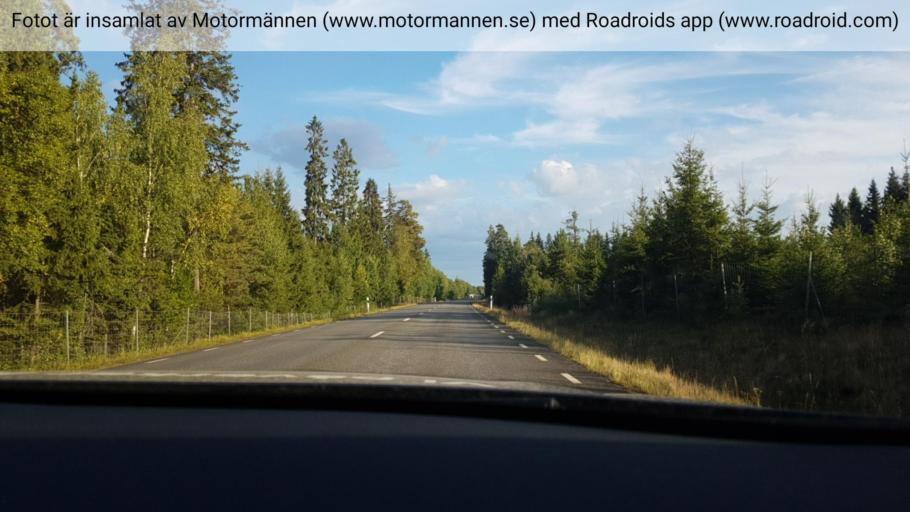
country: SE
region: Vaestra Goetaland
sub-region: Skara Kommun
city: Skara
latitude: 58.3522
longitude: 13.4299
